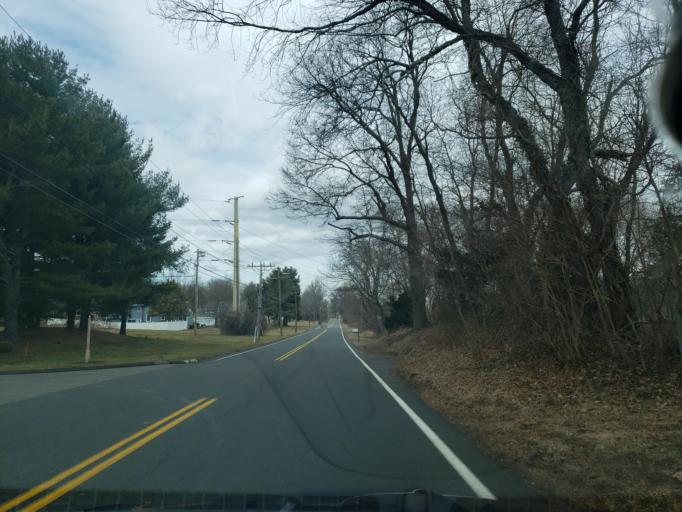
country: US
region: Connecticut
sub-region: Hartford County
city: Wethersfield
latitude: 41.6546
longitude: -72.6636
